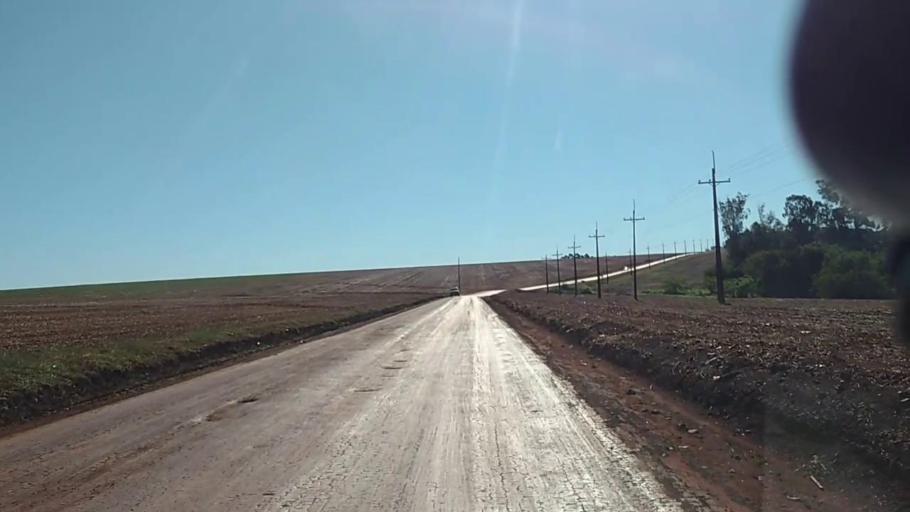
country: PY
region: Alto Parana
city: Naranjal
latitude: -25.9697
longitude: -55.2400
